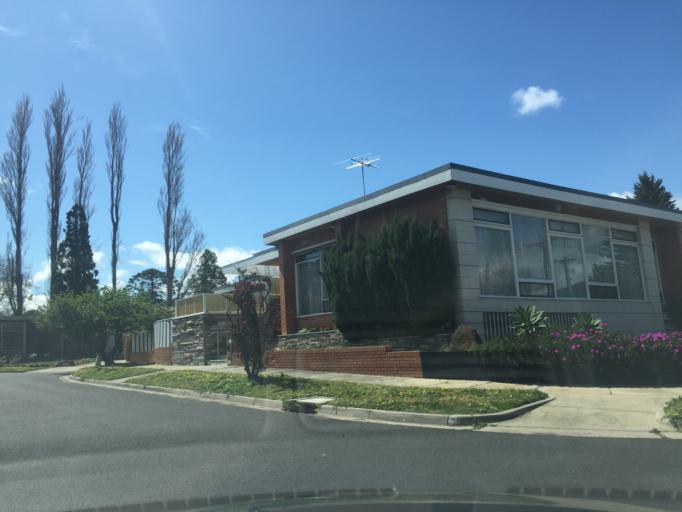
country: AU
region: Victoria
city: Balaclava
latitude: -37.8687
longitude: 145.0034
